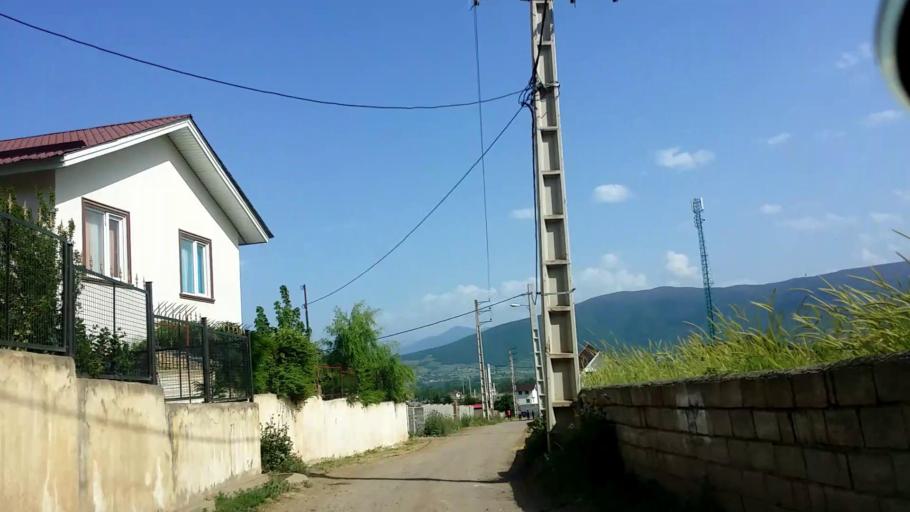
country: IR
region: Mazandaran
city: `Abbasabad
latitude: 36.5466
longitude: 51.1861
